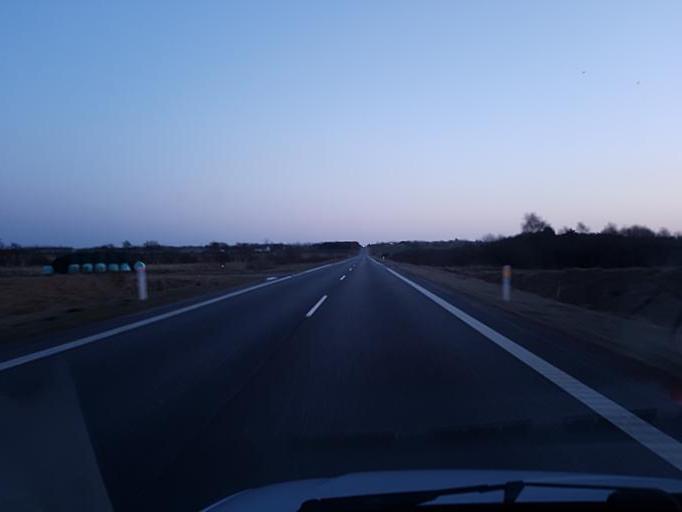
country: DK
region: Central Jutland
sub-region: Ringkobing-Skjern Kommune
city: Videbaek
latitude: 56.2101
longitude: 8.5859
